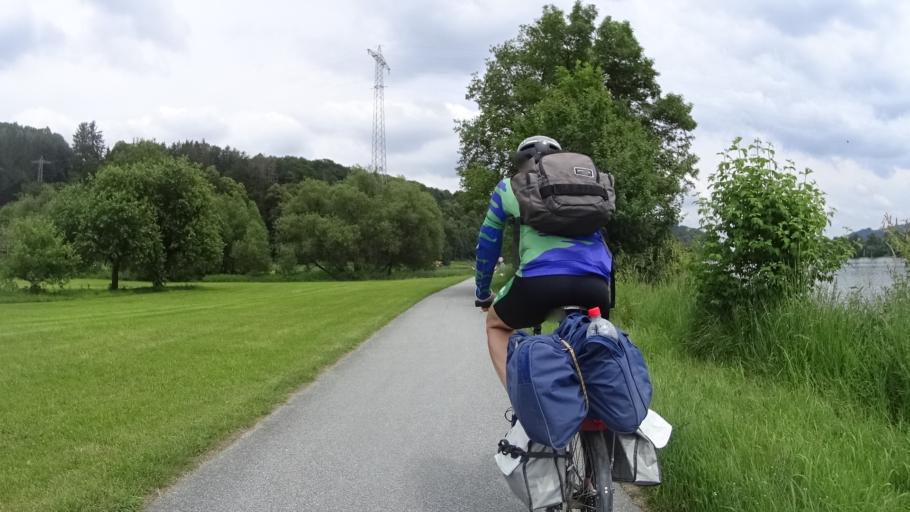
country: DE
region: Bavaria
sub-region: Lower Bavaria
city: Aicha vorm Wald
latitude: 48.6122
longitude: 13.2770
